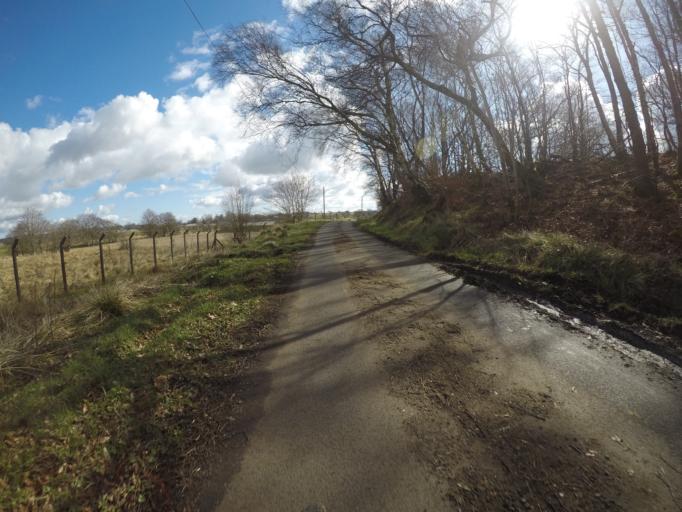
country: GB
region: Scotland
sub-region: North Ayrshire
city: Beith
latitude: 55.7175
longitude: -4.6286
